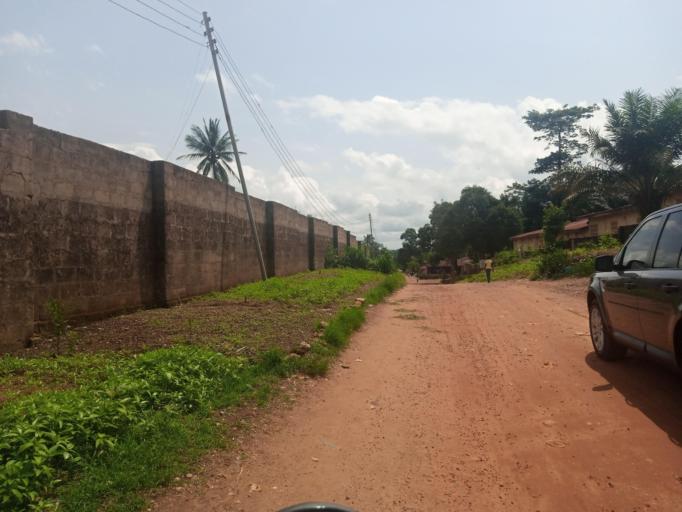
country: SL
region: Southern Province
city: Bo
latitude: 7.9708
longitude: -11.7339
